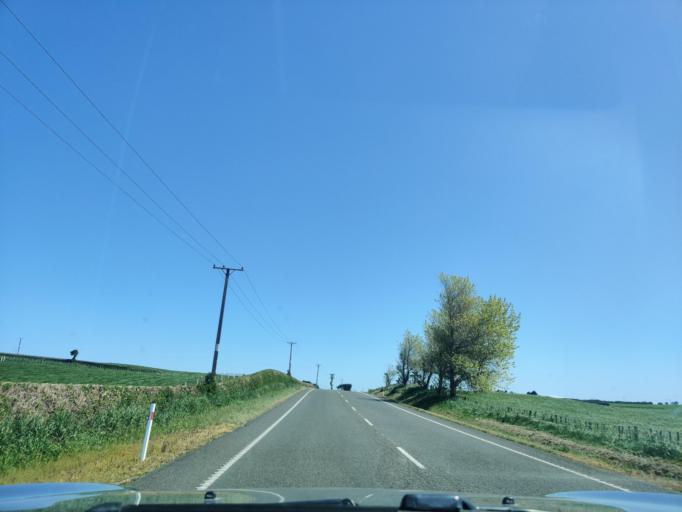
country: NZ
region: Taranaki
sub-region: South Taranaki District
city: Patea
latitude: -39.7771
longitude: 174.6853
